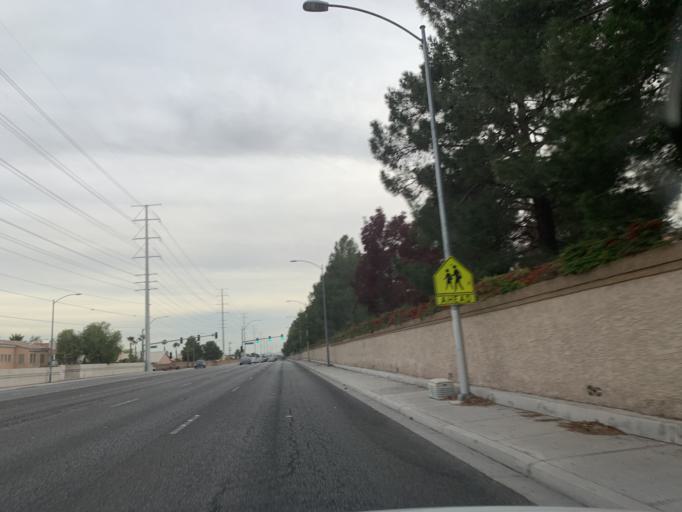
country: US
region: Nevada
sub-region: Clark County
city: Spring Valley
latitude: 36.1526
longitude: -115.2797
